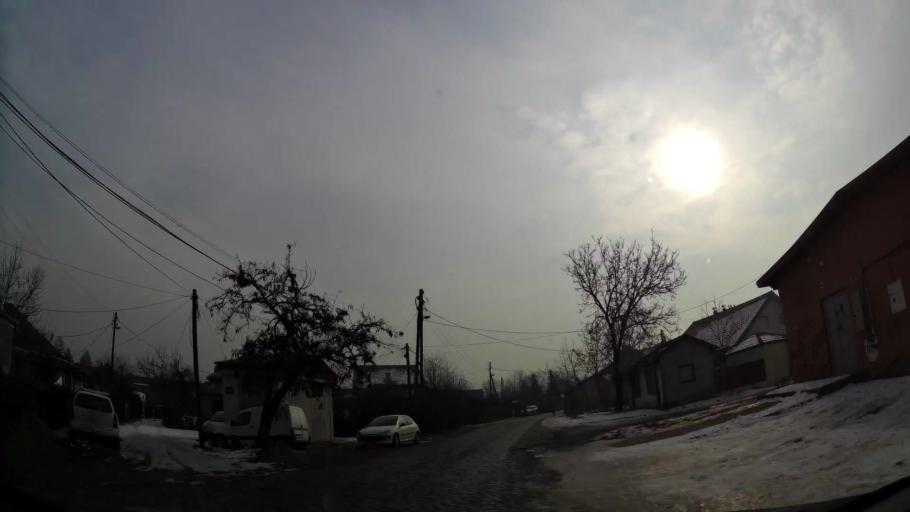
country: MK
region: Kisela Voda
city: Kisela Voda
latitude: 41.9959
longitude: 21.5042
